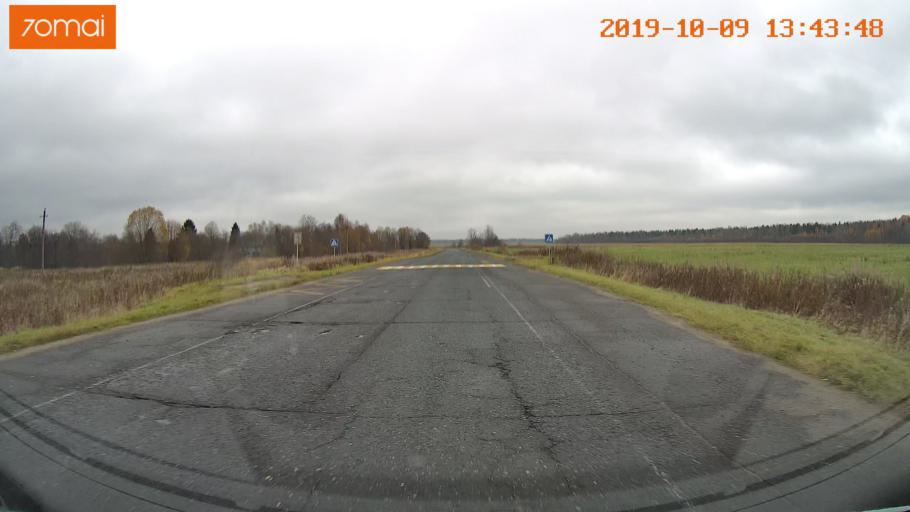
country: RU
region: Kostroma
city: Buy
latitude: 58.3602
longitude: 41.2042
